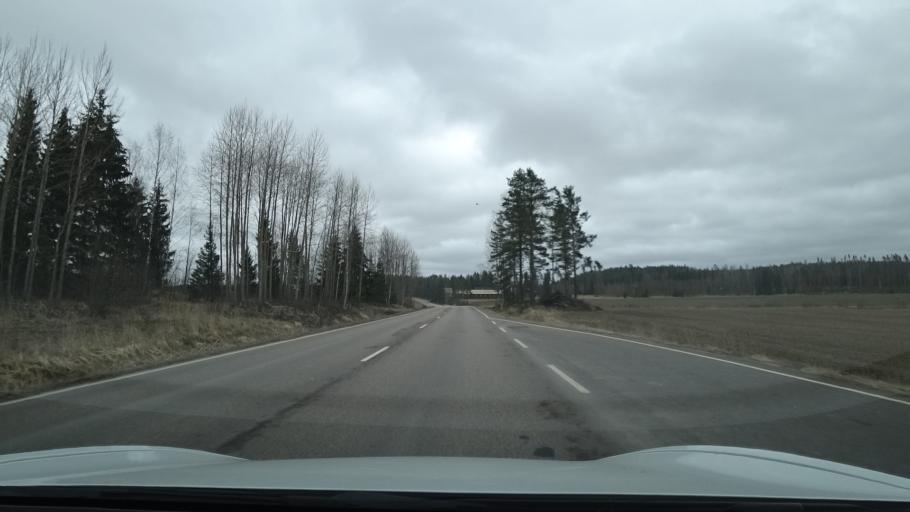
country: FI
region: Uusimaa
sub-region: Porvoo
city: Myrskylae
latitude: 60.7122
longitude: 25.9369
